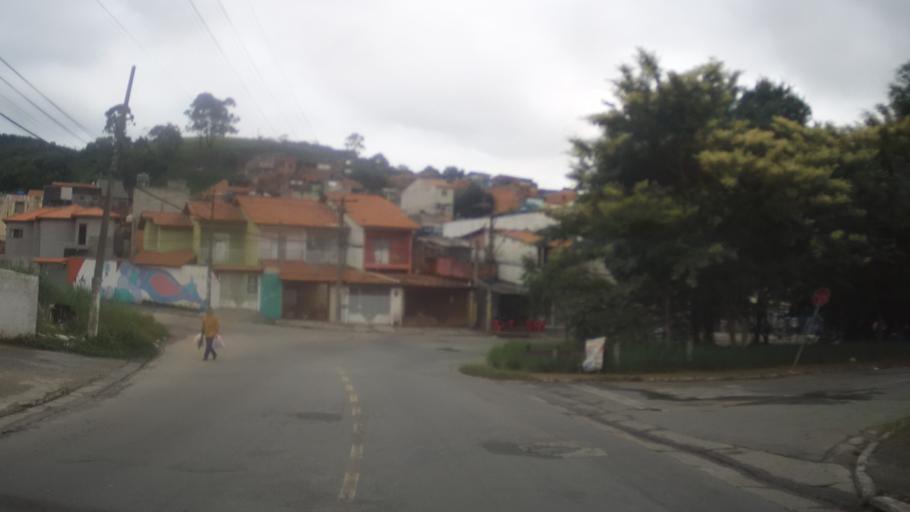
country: BR
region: Sao Paulo
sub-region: Guarulhos
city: Guarulhos
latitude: -23.4227
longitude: -46.5300
